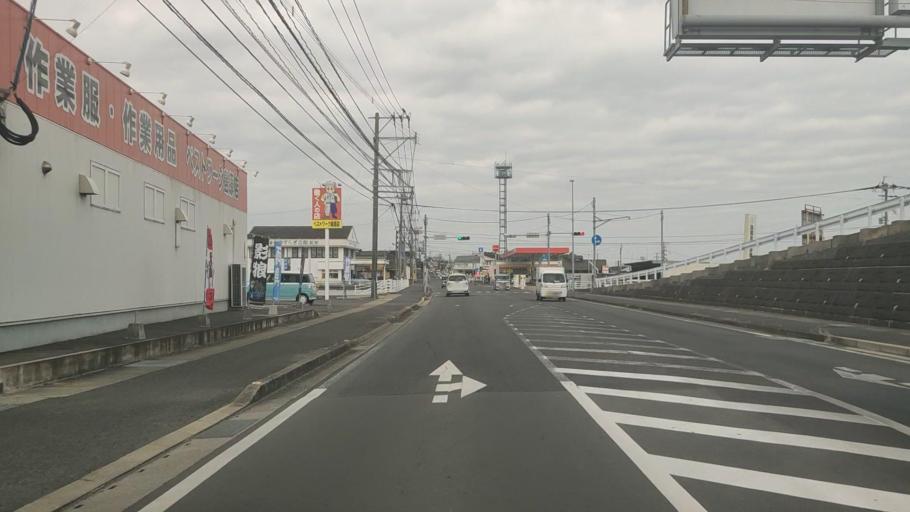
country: JP
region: Nagasaki
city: Shimabara
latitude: 32.8127
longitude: 130.3583
